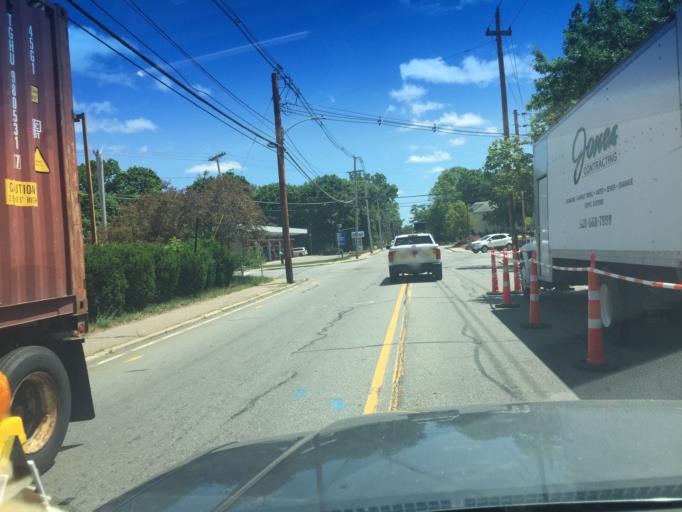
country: US
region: Massachusetts
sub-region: Bristol County
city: Mansfield
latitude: 42.0305
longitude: -71.2283
